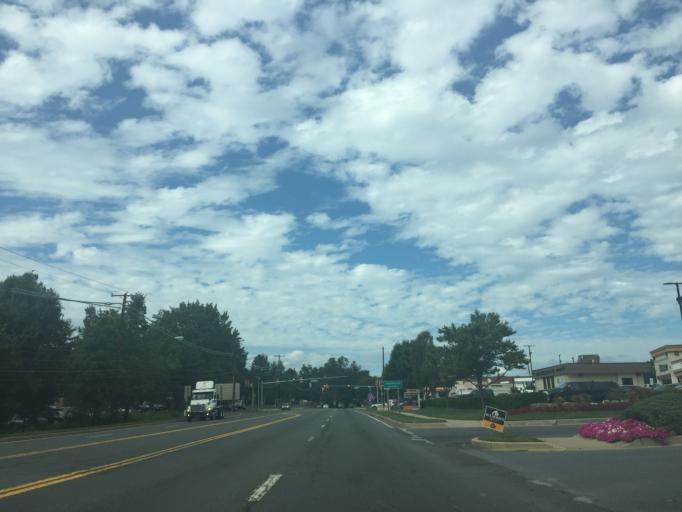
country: US
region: Maryland
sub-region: Montgomery County
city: Gaithersburg
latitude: 39.1438
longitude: -77.2204
